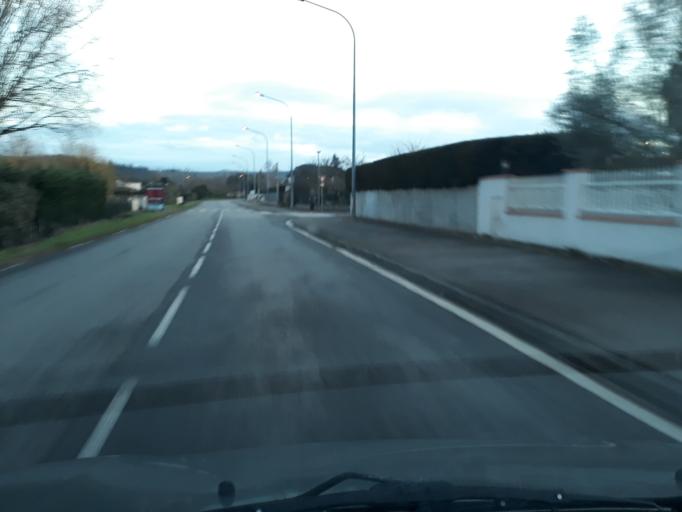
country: FR
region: Midi-Pyrenees
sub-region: Departement de la Haute-Garonne
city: Carbonne
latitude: 43.3073
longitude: 1.2294
